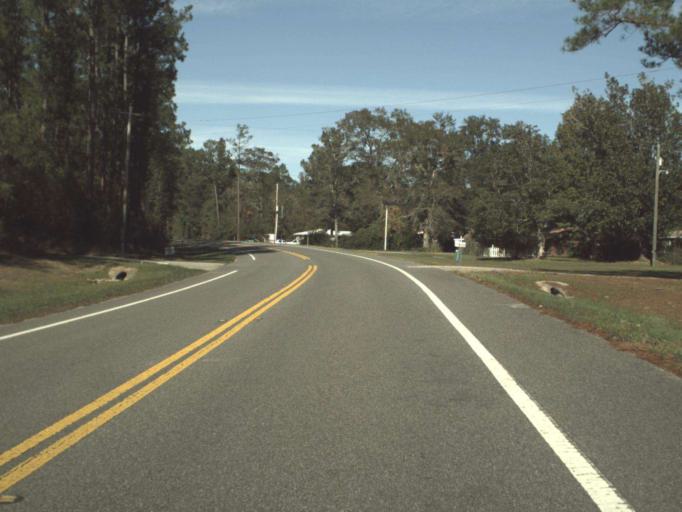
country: US
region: Florida
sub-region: Okaloosa County
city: Crestview
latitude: 30.8383
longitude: -86.7358
